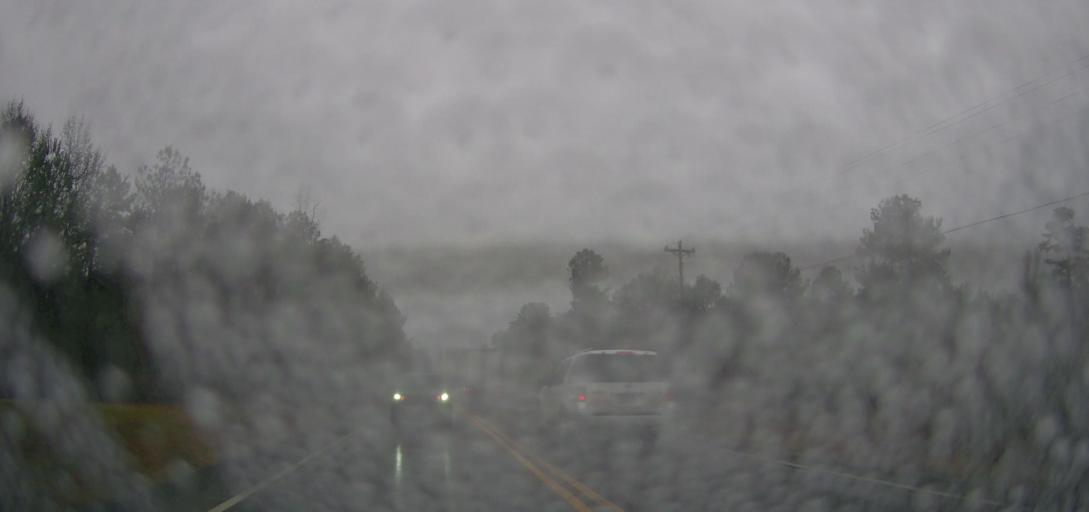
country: US
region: Georgia
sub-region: Putnam County
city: Eatonton
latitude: 33.2526
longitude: -83.4276
